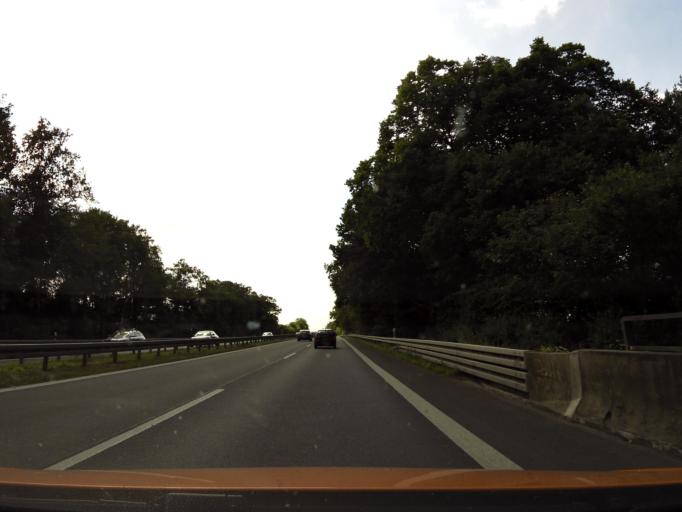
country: DE
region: Brandenburg
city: Marienwerder
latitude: 52.8675
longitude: 13.6833
